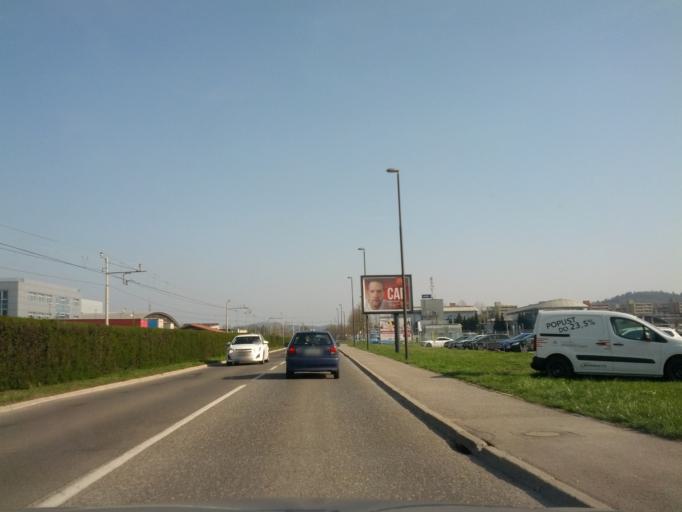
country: SI
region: Ljubljana
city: Ljubljana
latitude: 46.0839
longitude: 14.4828
